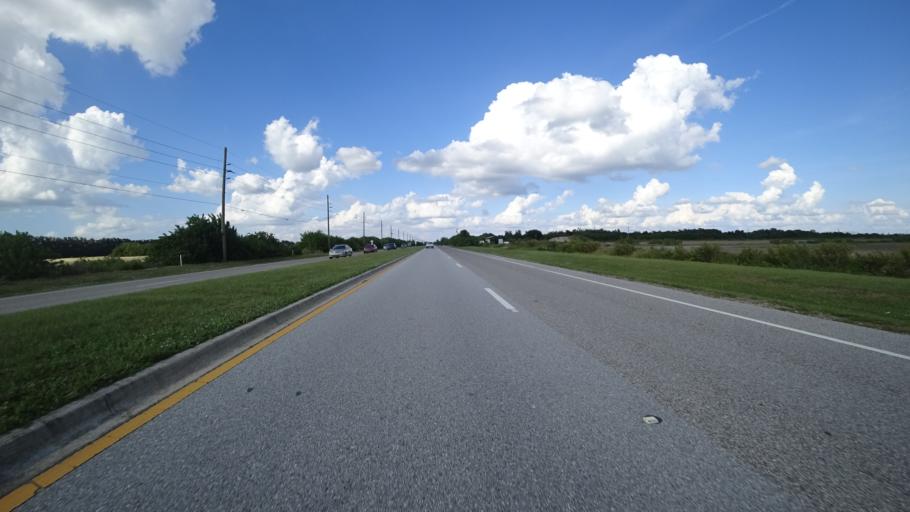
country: US
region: Florida
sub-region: Manatee County
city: Longboat Key
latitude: 27.4497
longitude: -82.6368
